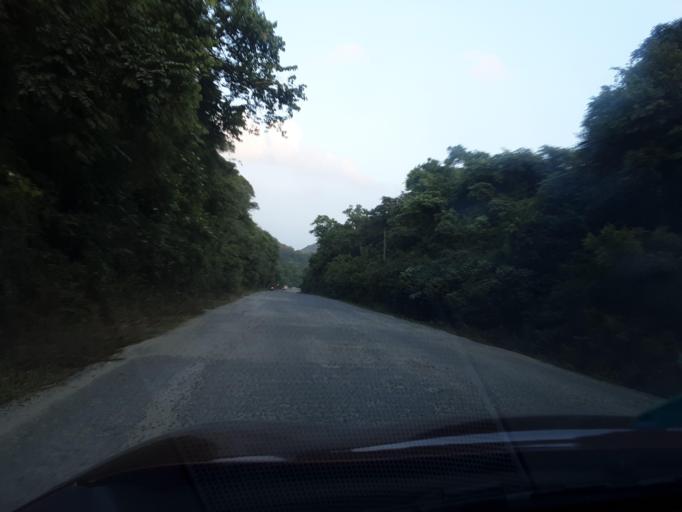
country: LK
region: Central
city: Dambulla
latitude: 7.8103
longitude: 80.7741
